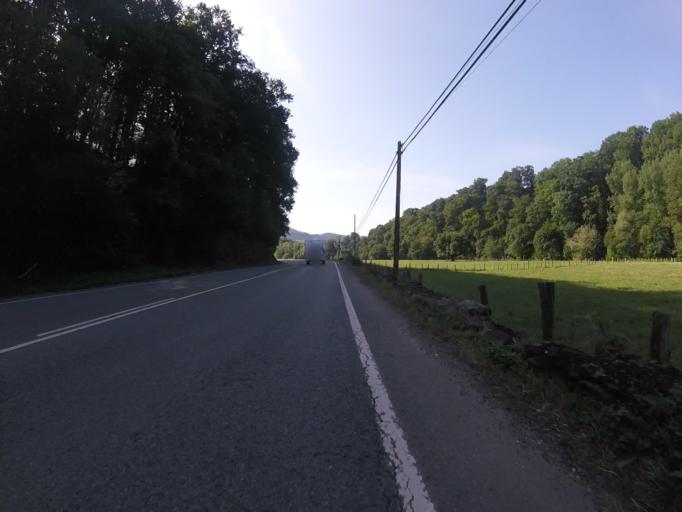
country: ES
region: Navarre
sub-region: Provincia de Navarra
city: Zugarramurdi
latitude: 43.1727
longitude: -1.4933
